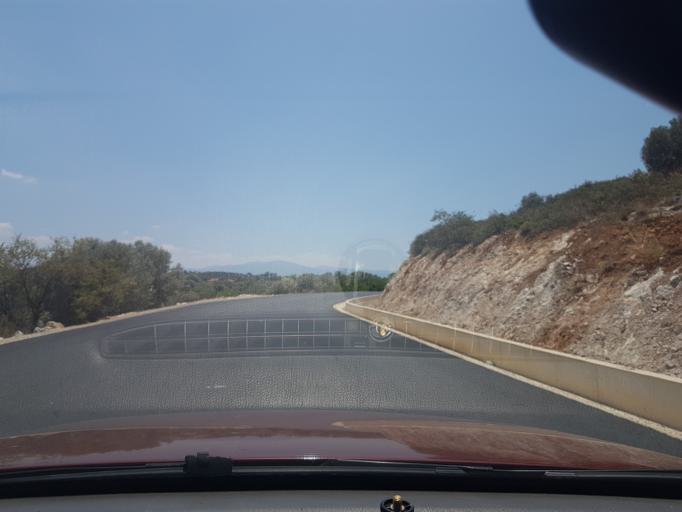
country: GR
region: Central Greece
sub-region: Nomos Evvoias
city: Filla
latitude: 38.4455
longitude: 23.6732
